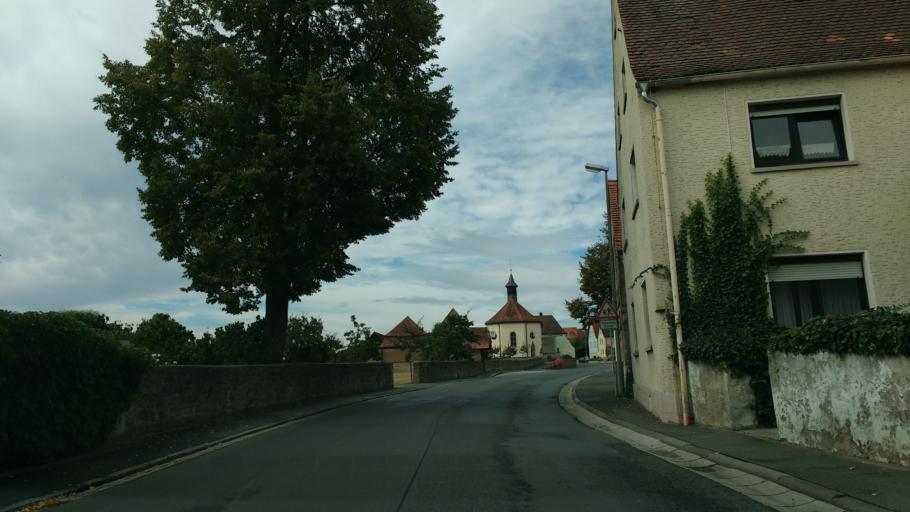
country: DE
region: Bavaria
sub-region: Upper Franconia
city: Schlusselfeld
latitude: 49.7597
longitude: 10.6099
